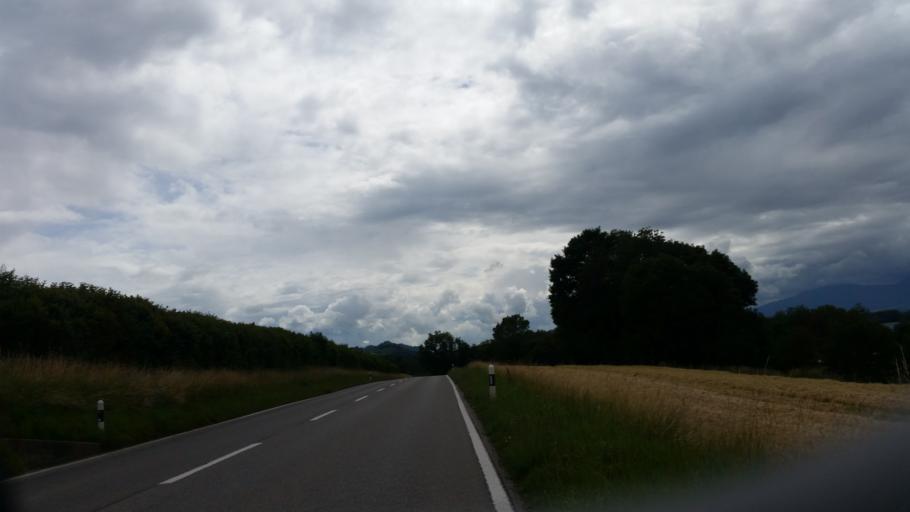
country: CH
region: Vaud
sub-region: Jura-Nord vaudois District
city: Yvonand
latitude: 46.8083
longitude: 6.7742
